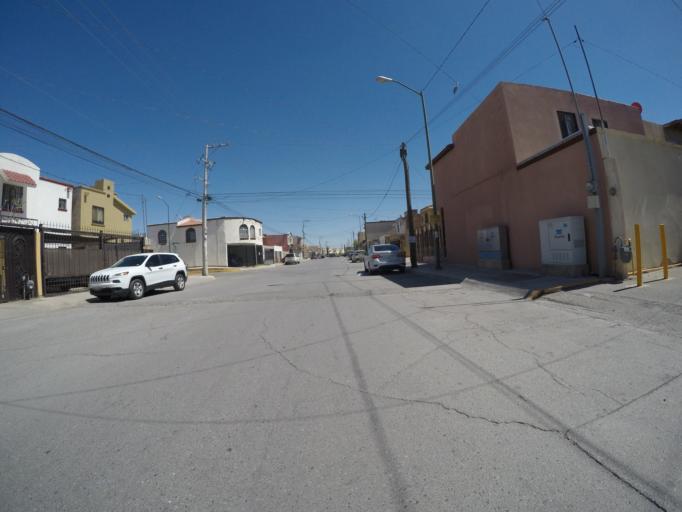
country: MX
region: Chihuahua
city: Ciudad Juarez
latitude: 31.6928
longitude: -106.4191
